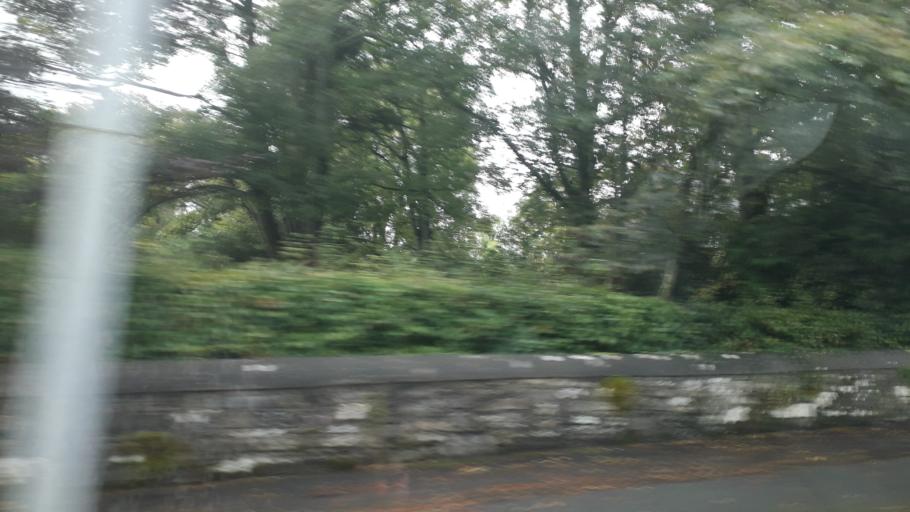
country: IE
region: Leinster
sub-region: An Longfort
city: Longford
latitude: 53.7335
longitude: -7.8007
